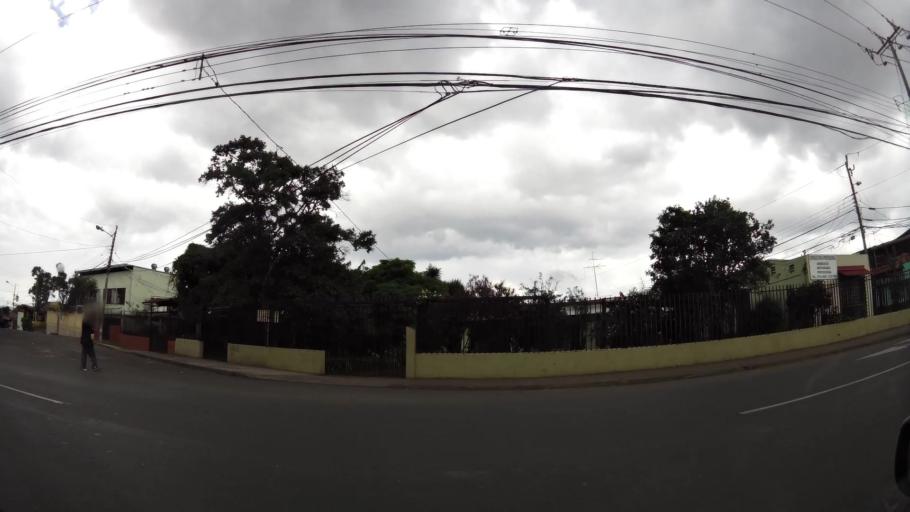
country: CR
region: San Jose
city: Alajuelita
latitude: 9.8995
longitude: -84.0881
